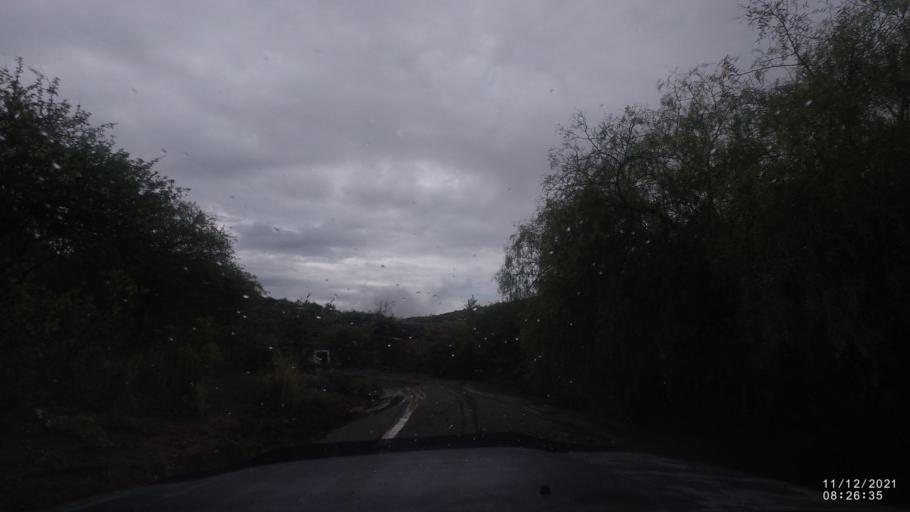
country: BO
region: Cochabamba
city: Tarata
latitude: -17.9381
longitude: -65.9304
